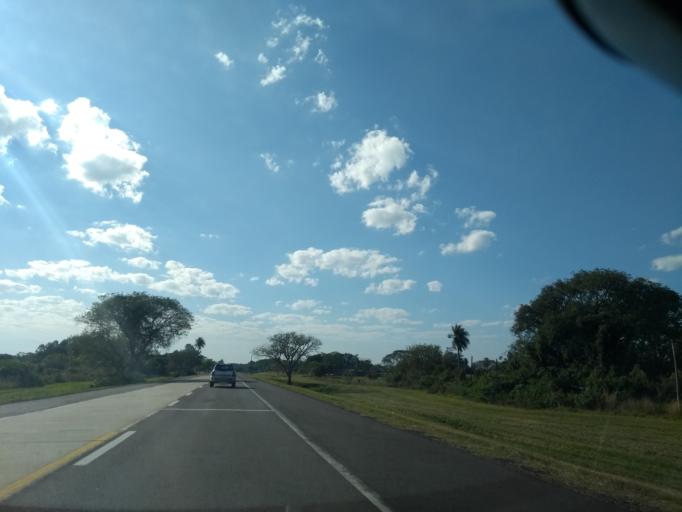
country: AR
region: Corrientes
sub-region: Departamento de San Cosme
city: San Cosme
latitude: -27.3675
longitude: -58.4673
